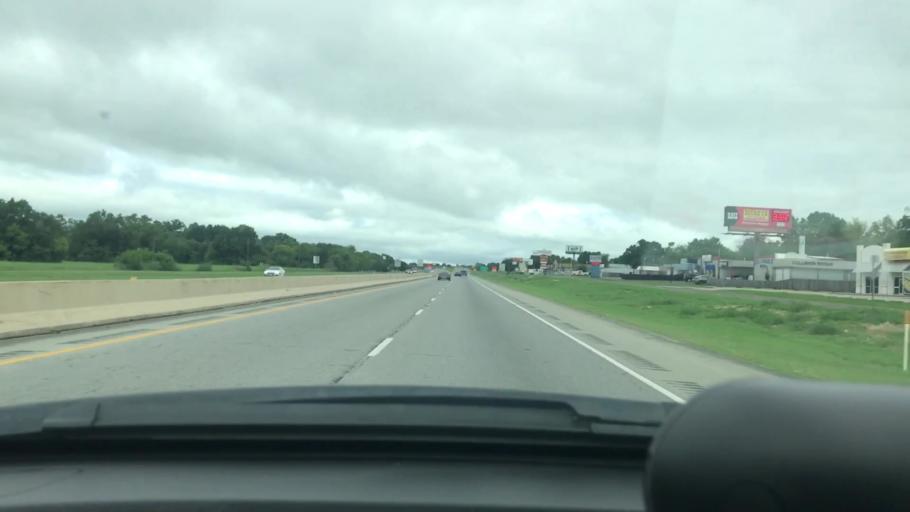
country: US
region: Texas
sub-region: Grayson County
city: Sherman
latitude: 33.6199
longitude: -96.6108
